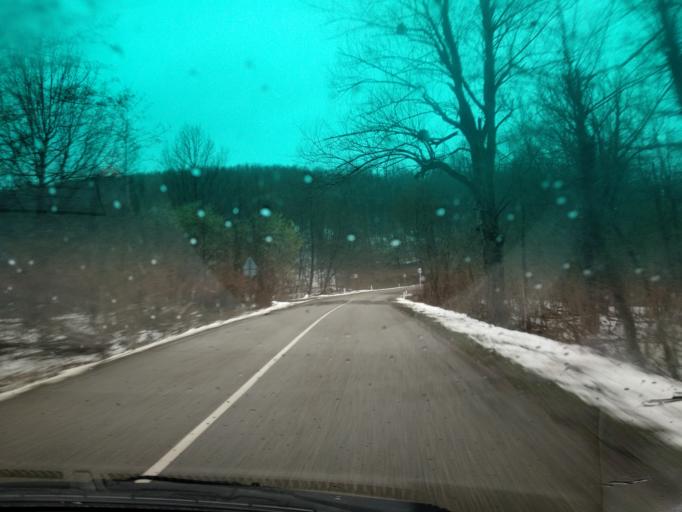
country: RU
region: Krasnodarskiy
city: Khadyzhensk
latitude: 44.2278
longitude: 39.3843
